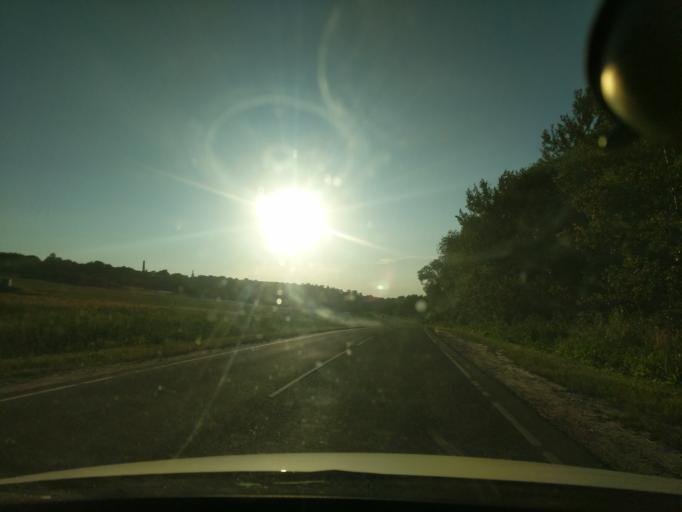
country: RU
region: Moskovskaya
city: Danki
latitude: 54.8467
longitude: 37.5023
